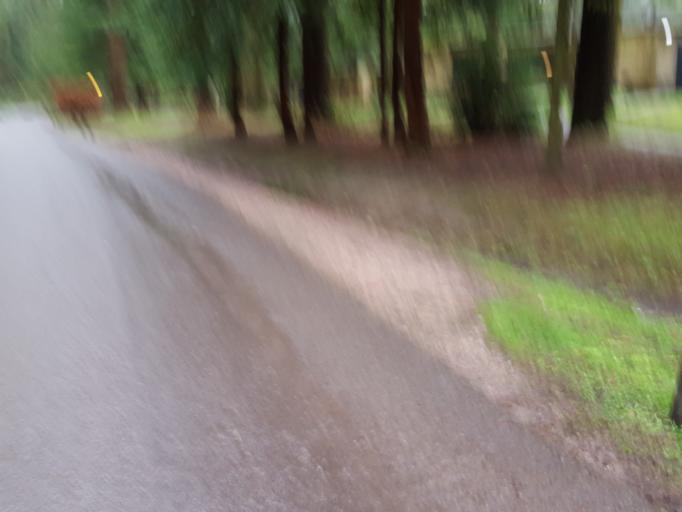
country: GB
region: England
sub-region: Wiltshire
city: Corsley
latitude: 51.1783
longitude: -2.2366
